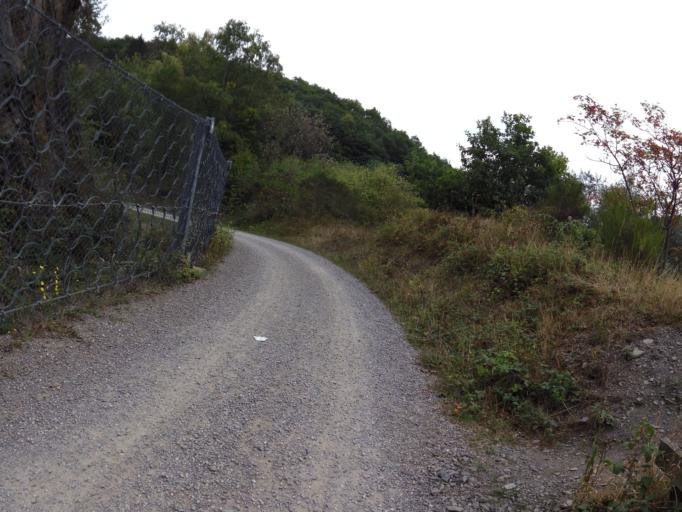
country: DE
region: North Rhine-Westphalia
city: Heimbach
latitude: 50.5943
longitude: 6.4520
